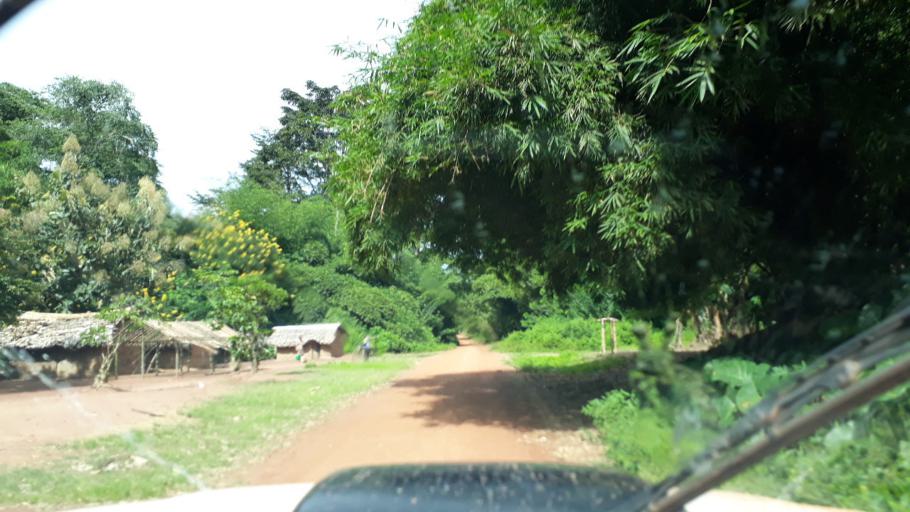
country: CD
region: Eastern Province
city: Buta
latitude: 2.8782
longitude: 24.4645
